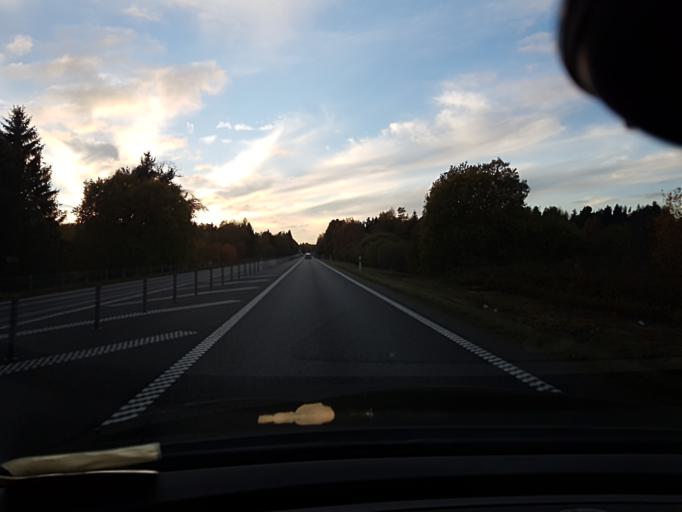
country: SE
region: Kronoberg
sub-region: Ljungby Kommun
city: Lagan
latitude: 56.8517
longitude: 14.0449
